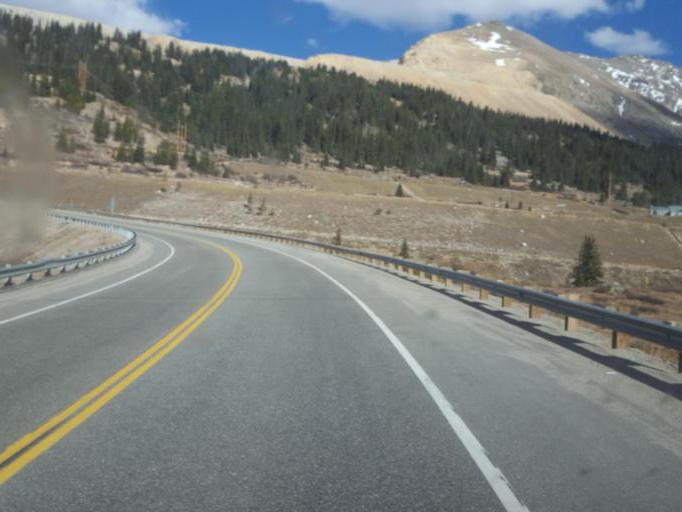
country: US
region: Colorado
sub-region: Lake County
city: Leadville
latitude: 39.3603
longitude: -106.1800
